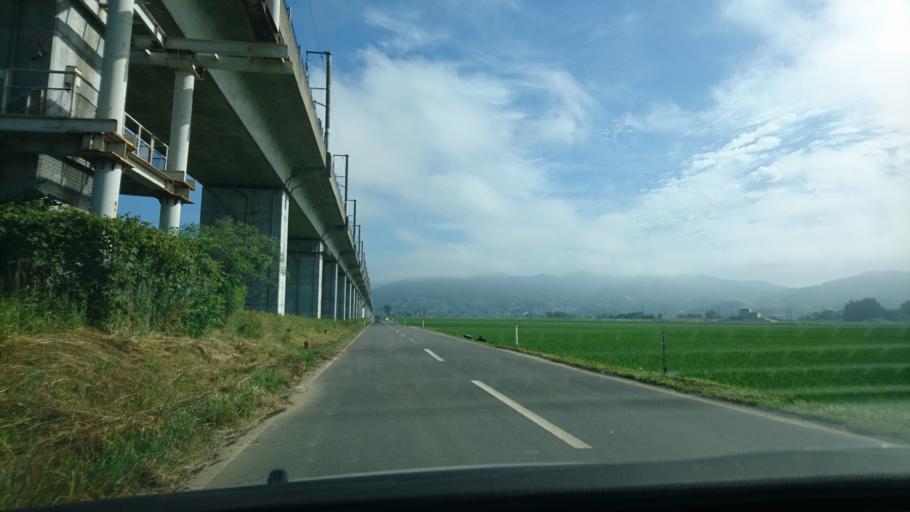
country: JP
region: Iwate
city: Ichinoseki
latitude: 38.9528
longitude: 141.1493
